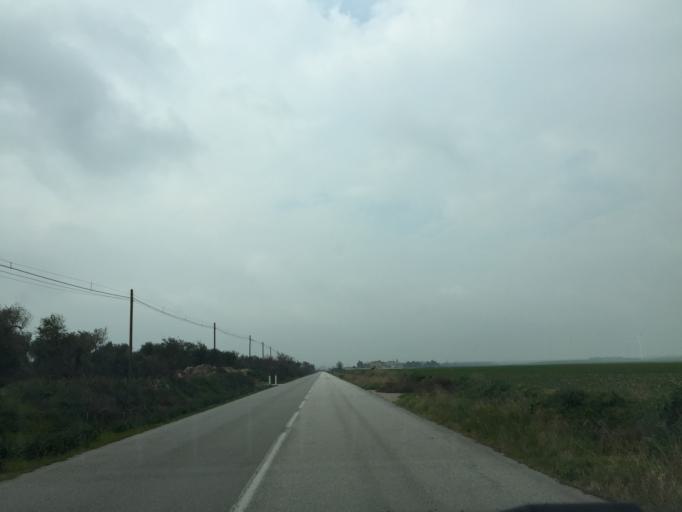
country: IT
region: Apulia
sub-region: Provincia di Foggia
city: Castelluccio dei Sauri
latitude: 41.3990
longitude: 15.4262
